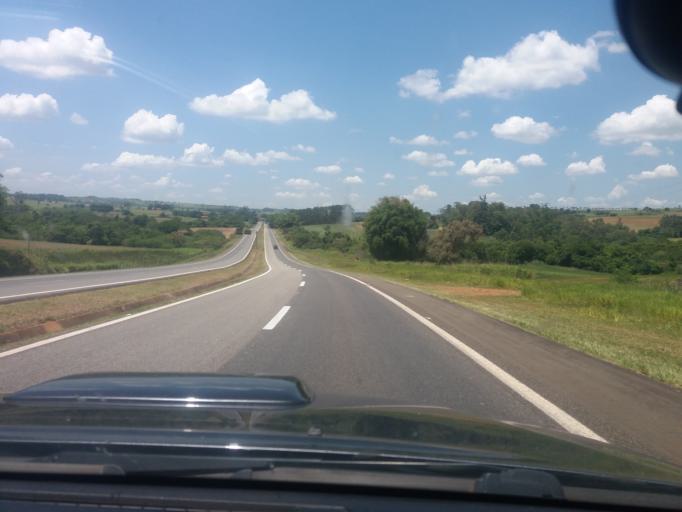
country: BR
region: Sao Paulo
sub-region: Tatui
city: Tatui
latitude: -23.4480
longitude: -47.9538
